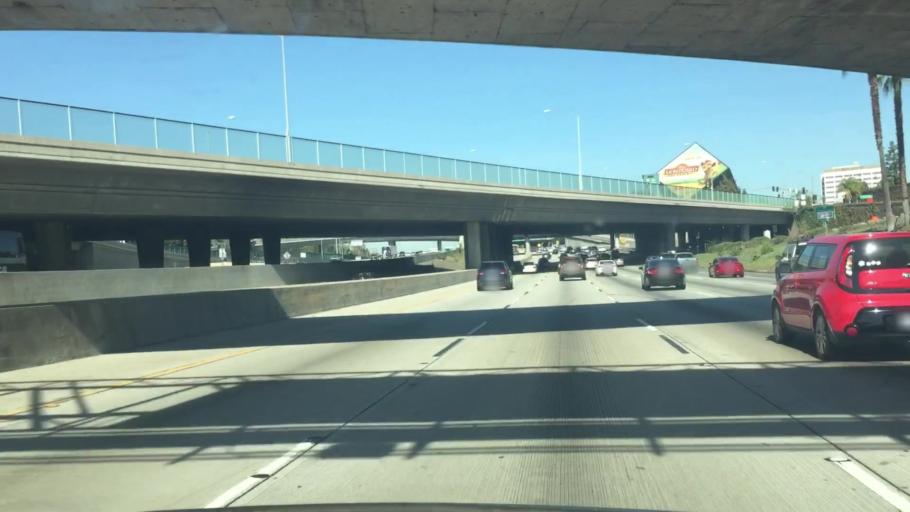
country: US
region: California
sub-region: Orange County
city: Santa Ana
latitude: 33.7670
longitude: -117.8668
